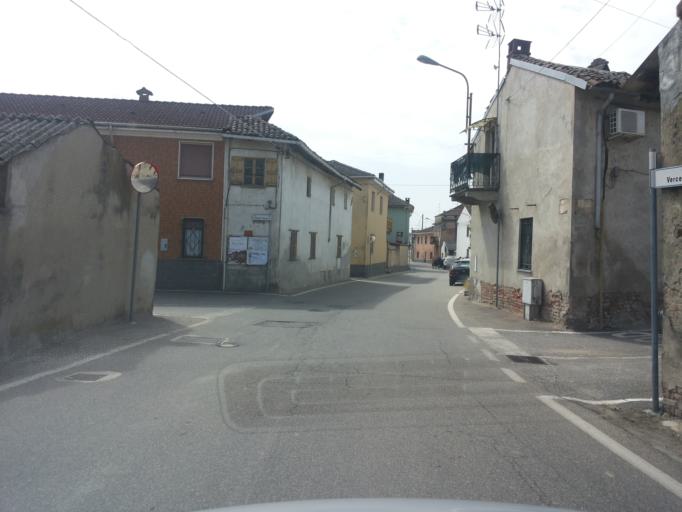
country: IT
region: Piedmont
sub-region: Provincia di Vercelli
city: Motta De Conti
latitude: 45.1944
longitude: 8.5183
